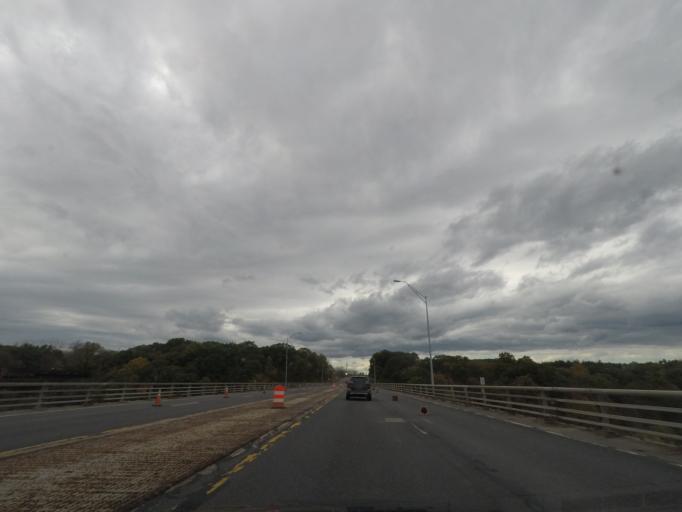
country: US
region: New York
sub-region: Rensselaer County
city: Castleton-on-Hudson
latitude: 42.5107
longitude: -73.7774
